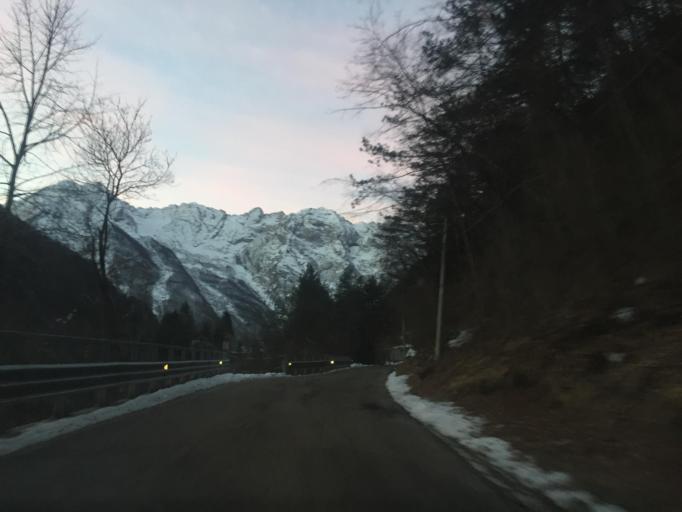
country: IT
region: Friuli Venezia Giulia
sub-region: Provincia di Udine
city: Prato
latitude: 46.3608
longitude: 13.2962
